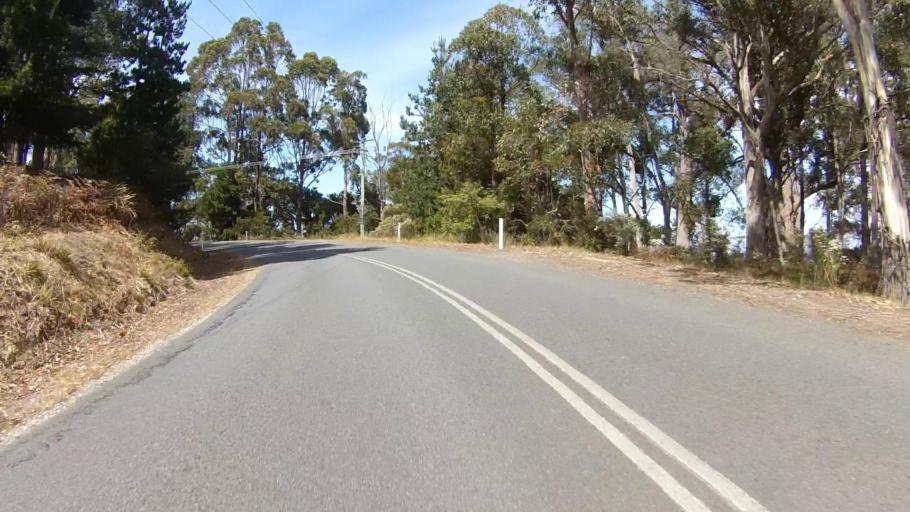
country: AU
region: Tasmania
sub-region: Huon Valley
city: Cygnet
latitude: -43.2273
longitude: 147.1274
